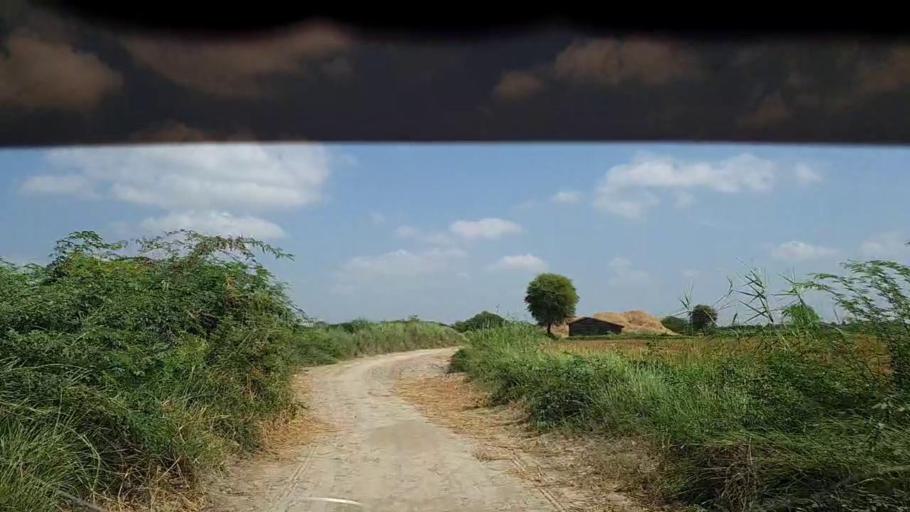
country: PK
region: Sindh
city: Kadhan
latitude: 24.5832
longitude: 68.9691
